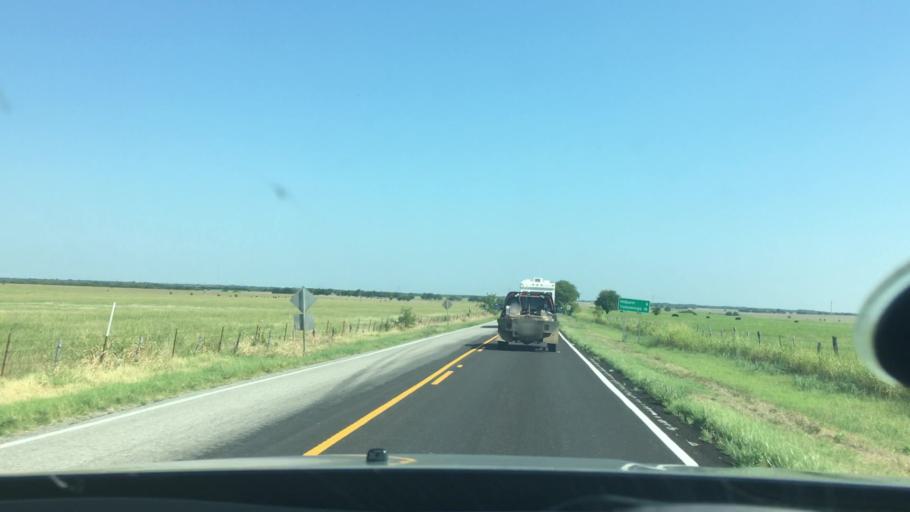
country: US
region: Oklahoma
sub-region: Johnston County
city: Tishomingo
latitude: 34.1456
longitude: -96.5044
